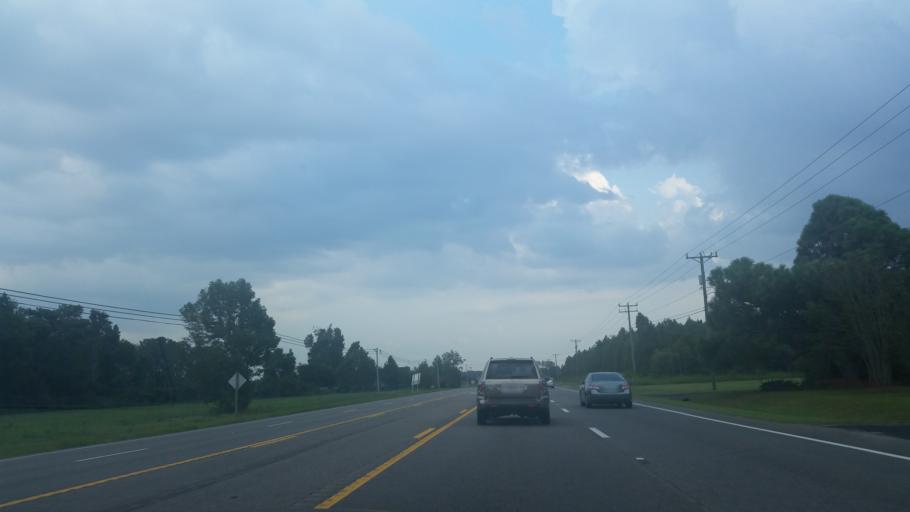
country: US
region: North Carolina
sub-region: Dare County
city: Southern Shores
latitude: 36.1998
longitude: -75.8648
